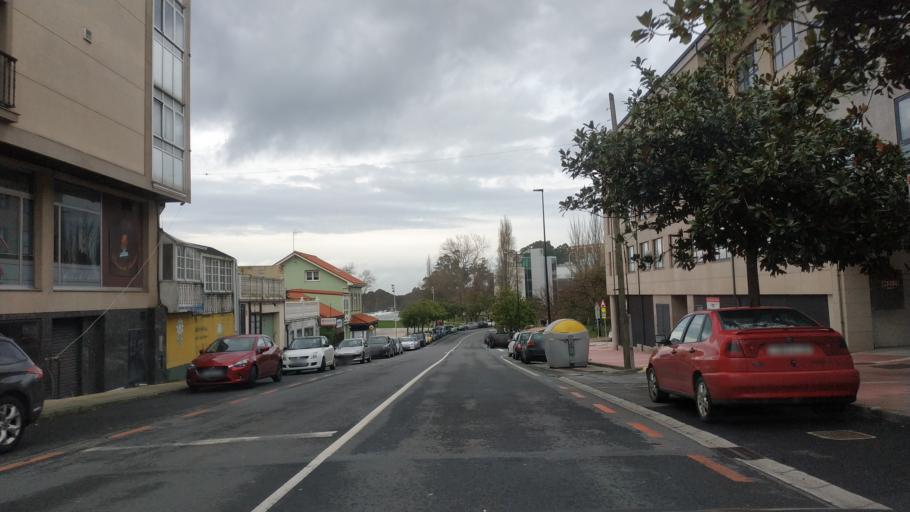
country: ES
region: Galicia
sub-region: Provincia da Coruna
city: Oleiros
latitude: 43.3468
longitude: -8.3457
